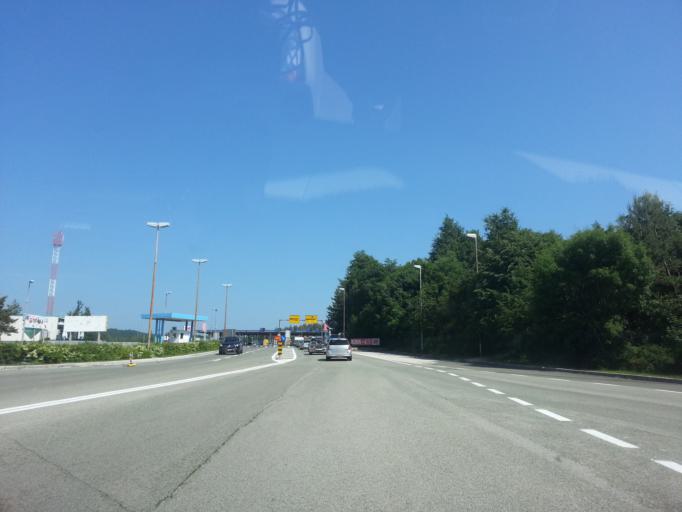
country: SI
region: Ilirska Bistrica
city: Ilirska Bistrica
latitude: 45.4886
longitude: 14.2787
